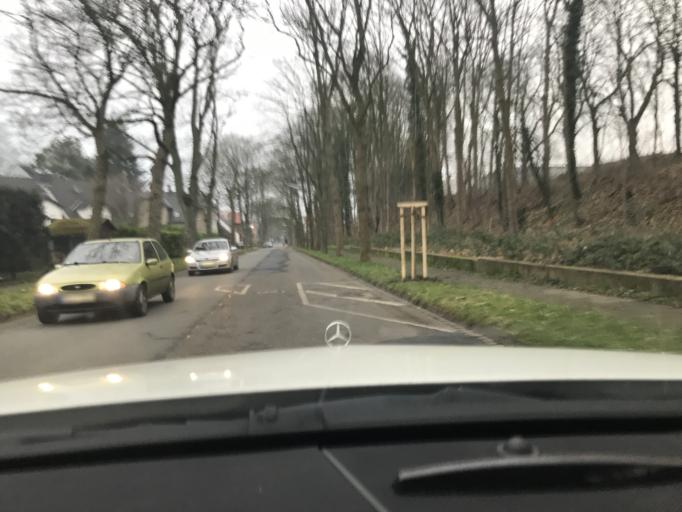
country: DE
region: North Rhine-Westphalia
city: Waltrop
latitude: 51.6198
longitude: 7.4216
